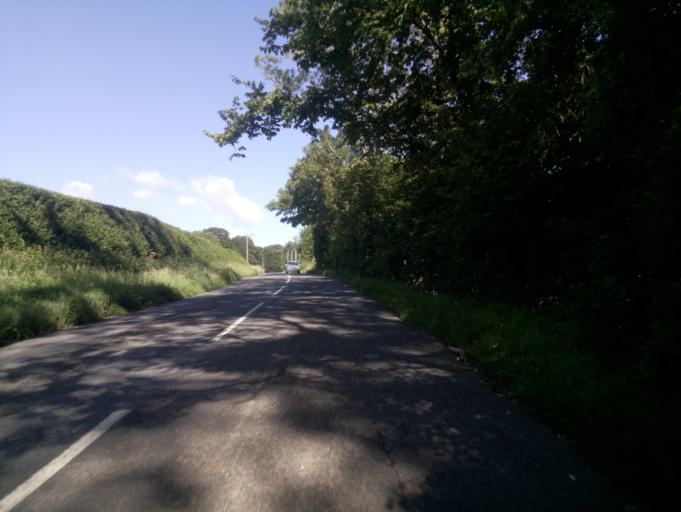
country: GB
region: England
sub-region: Herefordshire
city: Linton
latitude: 51.9343
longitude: -2.5044
